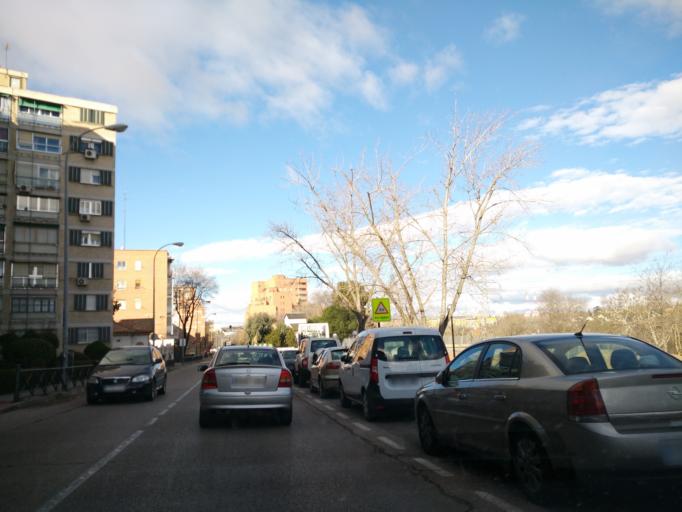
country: ES
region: Madrid
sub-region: Provincia de Madrid
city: Latina
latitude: 40.3992
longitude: -3.7693
